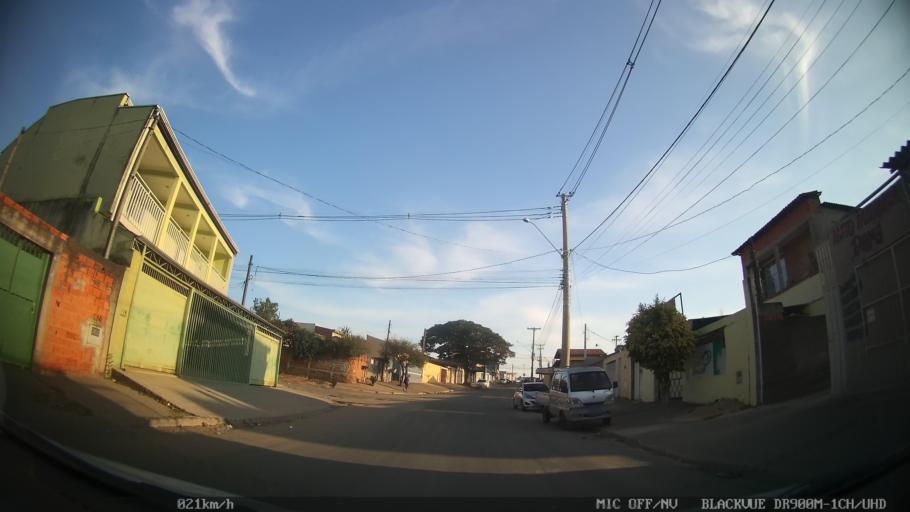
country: BR
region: Sao Paulo
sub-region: Campinas
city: Campinas
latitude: -22.9892
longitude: -47.1174
